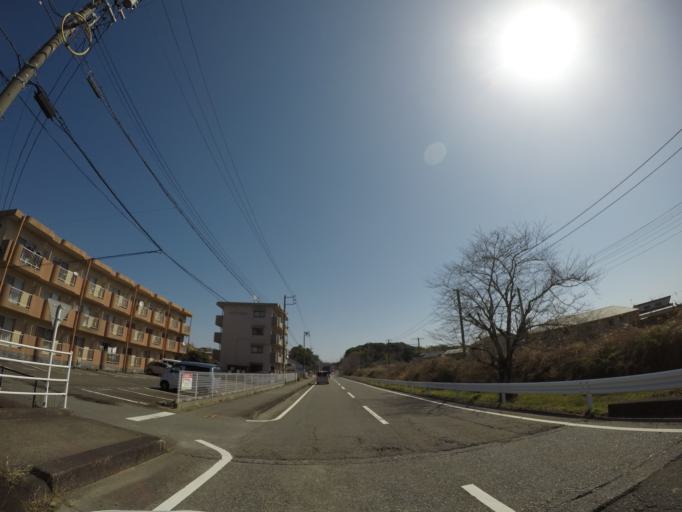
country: JP
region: Shizuoka
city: Kakegawa
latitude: 34.7610
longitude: 138.0755
